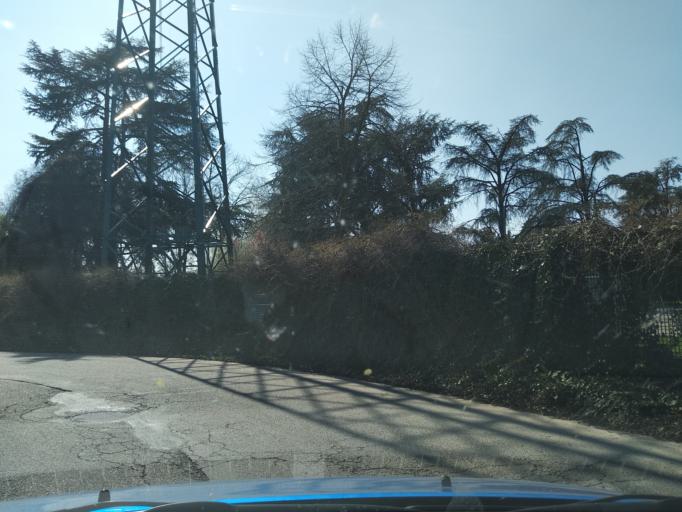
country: IT
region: Emilia-Romagna
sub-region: Provincia di Reggio Emilia
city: Reggio nell'Emilia
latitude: 44.6966
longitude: 10.6100
